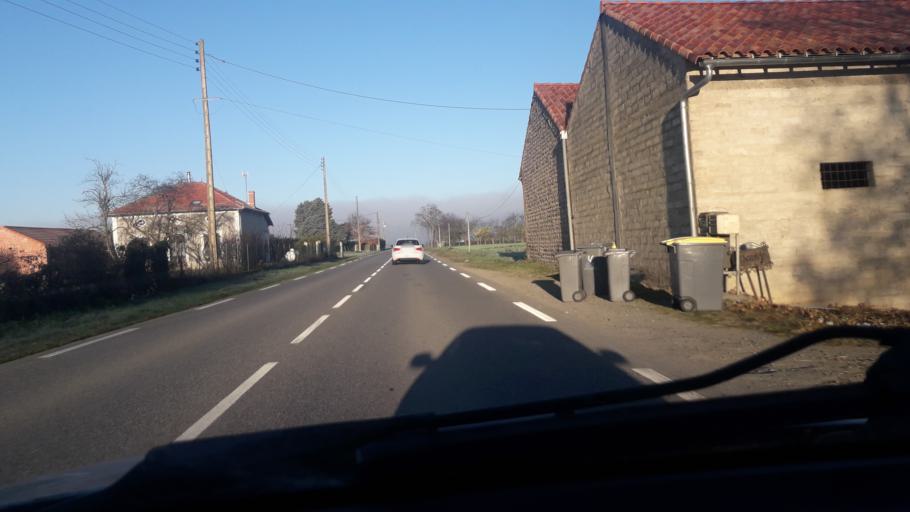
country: FR
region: Midi-Pyrenees
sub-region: Departement de la Haute-Garonne
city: Carbonne
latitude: 43.2980
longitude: 1.1967
